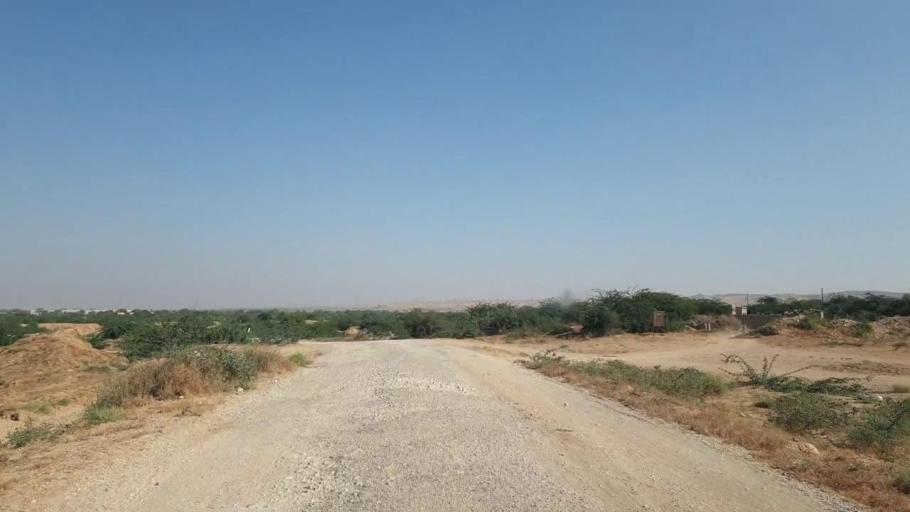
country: PK
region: Sindh
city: Gharo
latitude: 25.1738
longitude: 67.7326
